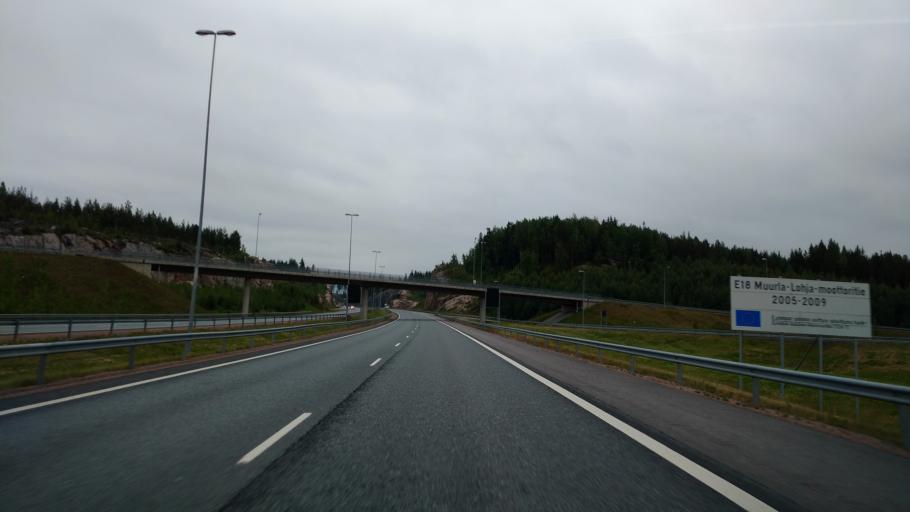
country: FI
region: Varsinais-Suomi
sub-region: Salo
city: Muurla
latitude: 60.3804
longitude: 23.3175
